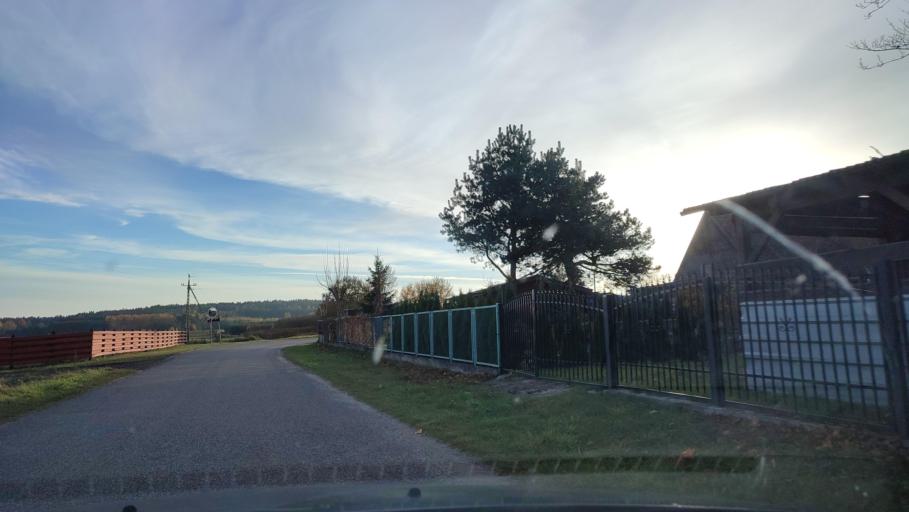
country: PL
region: Masovian Voivodeship
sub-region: Powiat przasnyski
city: Chorzele
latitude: 53.3386
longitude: 20.7520
